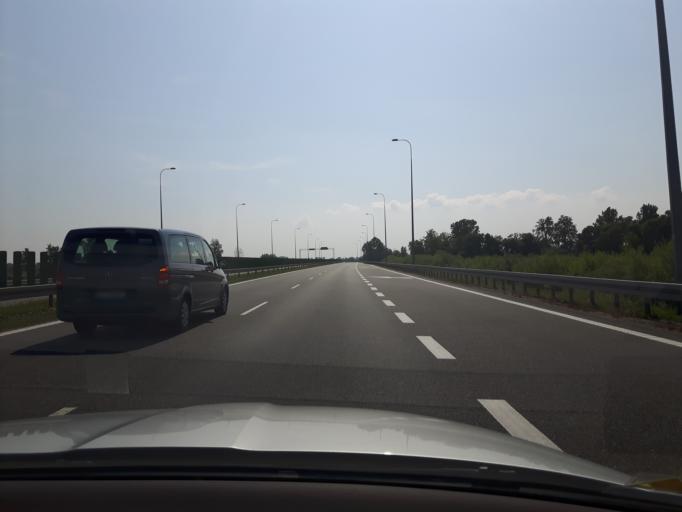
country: PL
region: Pomeranian Voivodeship
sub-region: Powiat gdanski
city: Cedry Wielkie
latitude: 54.2948
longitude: 18.8211
